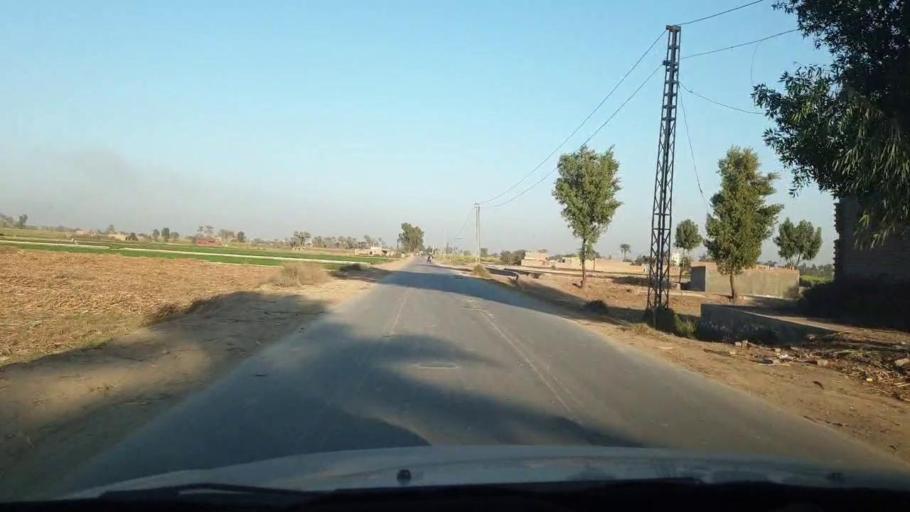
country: PK
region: Sindh
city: Ghotki
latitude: 28.0002
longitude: 69.2890
